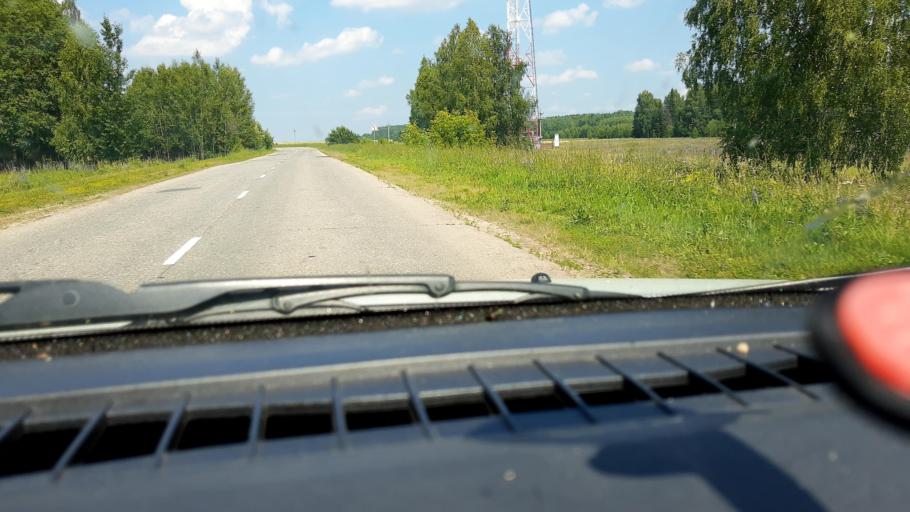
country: RU
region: Nizjnij Novgorod
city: Sharanga
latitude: 57.0569
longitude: 46.5460
